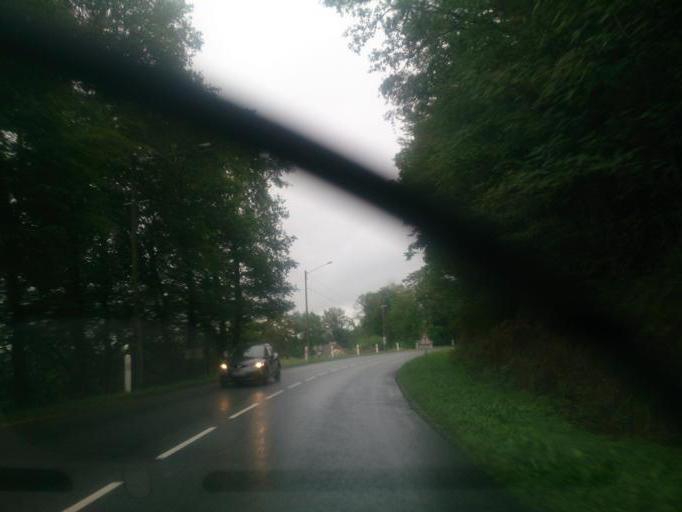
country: FR
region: Limousin
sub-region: Departement de la Correze
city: Malemort-sur-Correze
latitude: 45.1804
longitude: 1.5715
